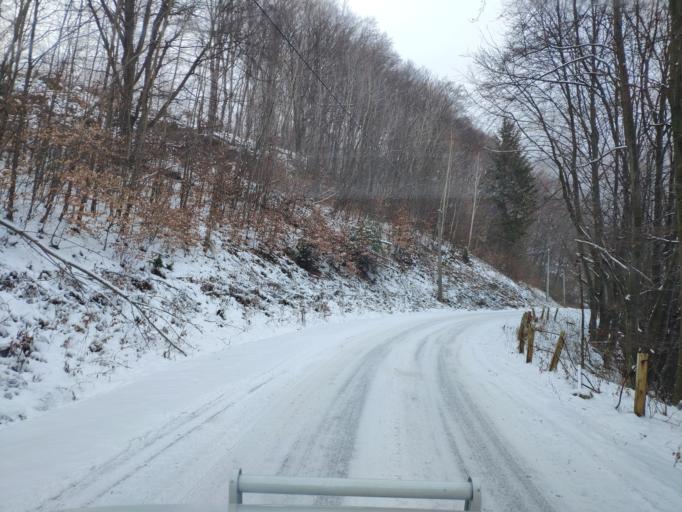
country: SK
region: Kosicky
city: Gelnica
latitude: 48.7541
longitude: 21.0016
